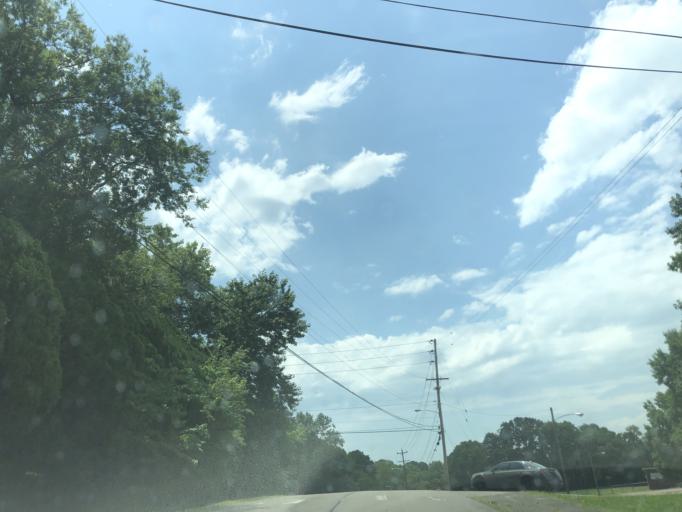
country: US
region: Tennessee
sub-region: Davidson County
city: Lakewood
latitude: 36.1559
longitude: -86.6520
